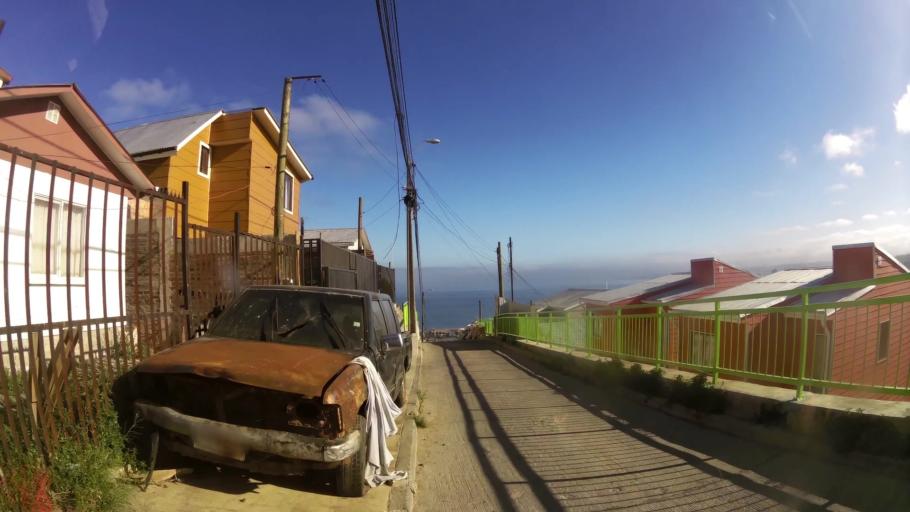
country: CL
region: Valparaiso
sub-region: Provincia de Valparaiso
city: Valparaiso
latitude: -33.0592
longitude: -71.6113
